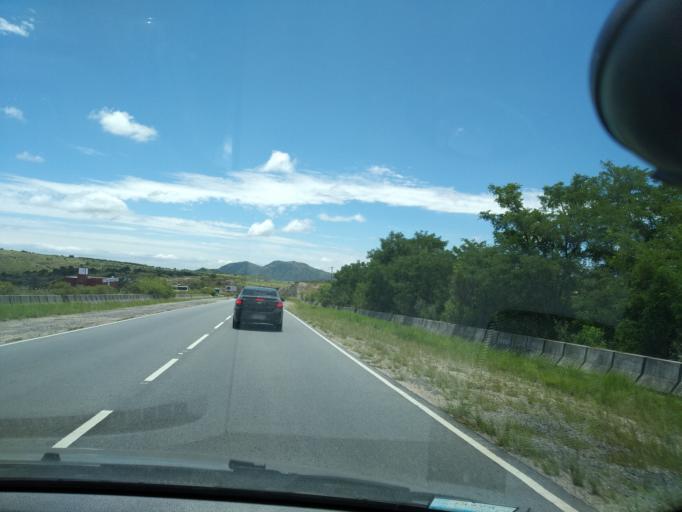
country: AR
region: Cordoba
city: Cuesta Blanca
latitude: -31.5805
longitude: -64.6082
